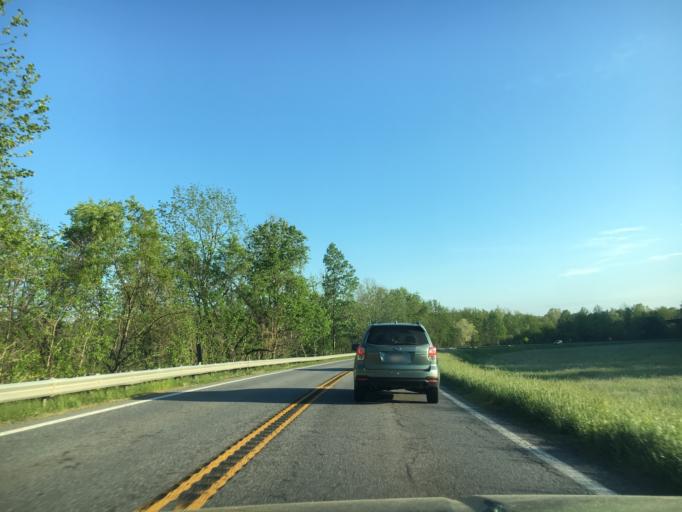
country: US
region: Virginia
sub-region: Campbell County
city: Rustburg
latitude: 37.2989
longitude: -79.1110
